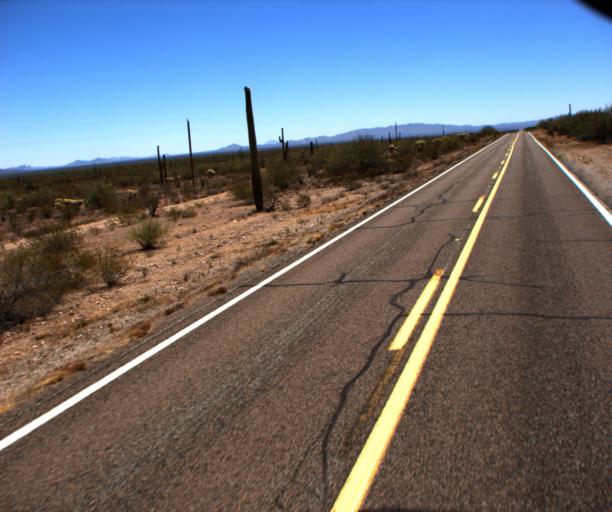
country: US
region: Arizona
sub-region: Pima County
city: Ajo
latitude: 32.2046
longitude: -112.5314
